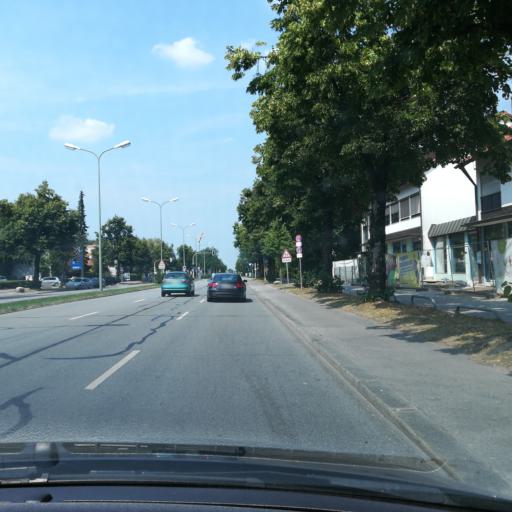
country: DE
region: Bavaria
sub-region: Upper Bavaria
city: Neuried
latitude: 48.1202
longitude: 11.5027
